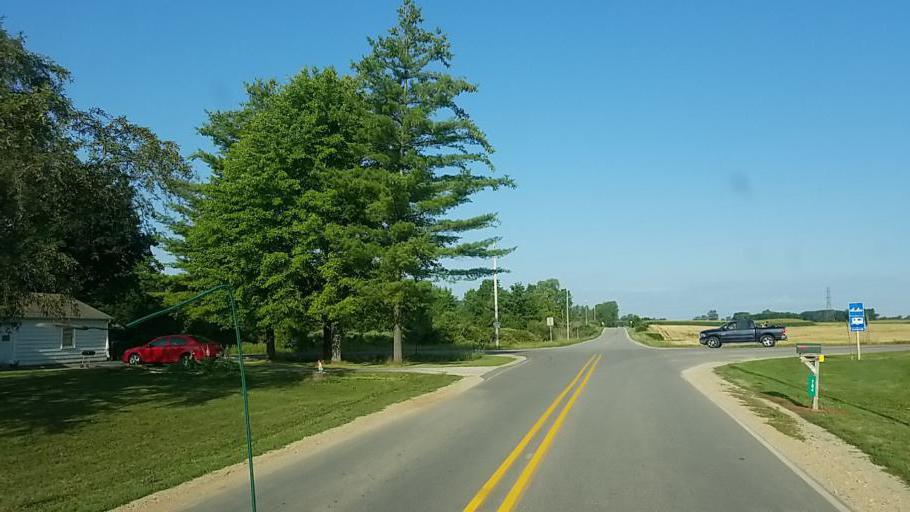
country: US
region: Michigan
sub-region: Newaygo County
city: Newaygo
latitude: 43.3512
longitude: -85.8201
